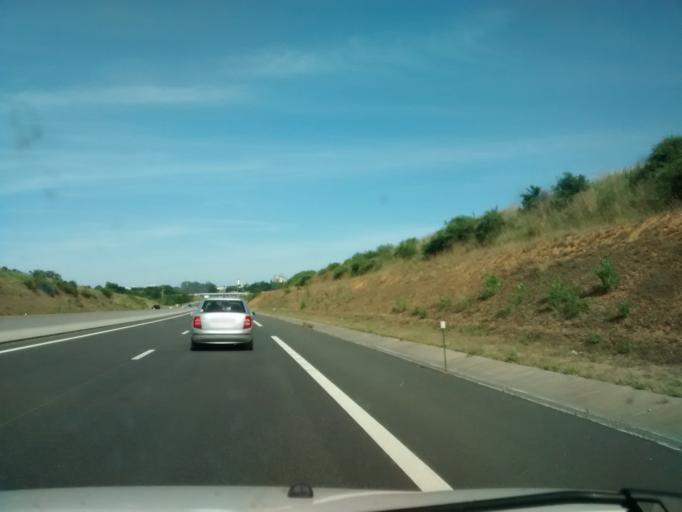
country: FR
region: Brittany
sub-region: Departement d'Ille-et-Vilaine
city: Vezin-le-Coquet
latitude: 48.1256
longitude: -1.7349
